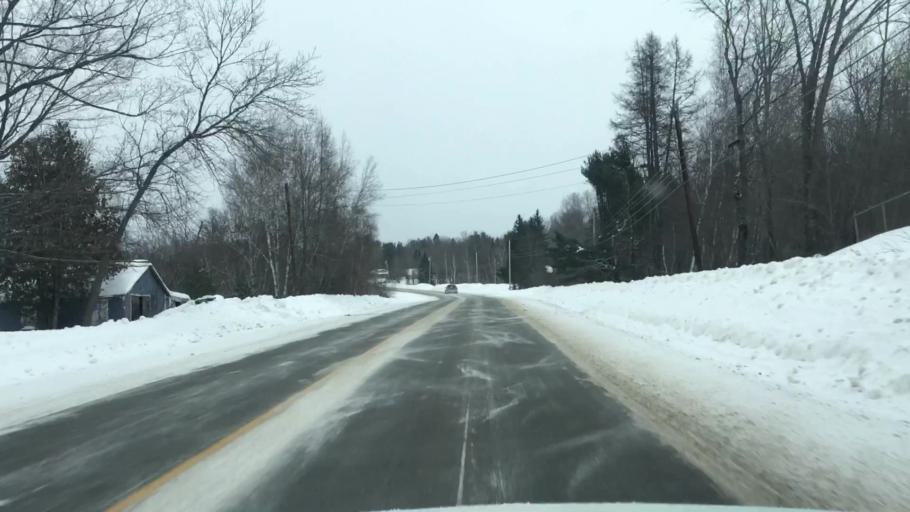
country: US
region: Maine
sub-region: Penobscot County
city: Lincoln
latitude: 45.4033
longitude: -68.4890
